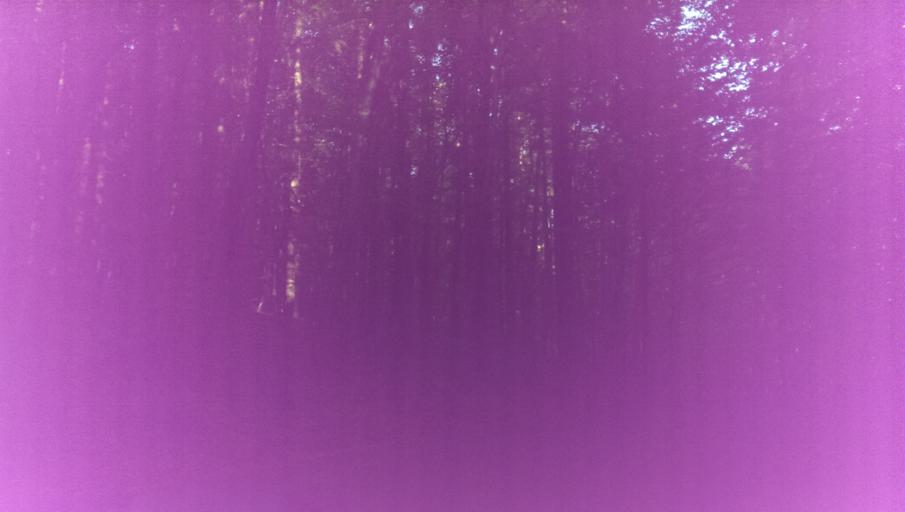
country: CZ
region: Zlin
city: Korycany
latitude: 49.0935
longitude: 17.1989
